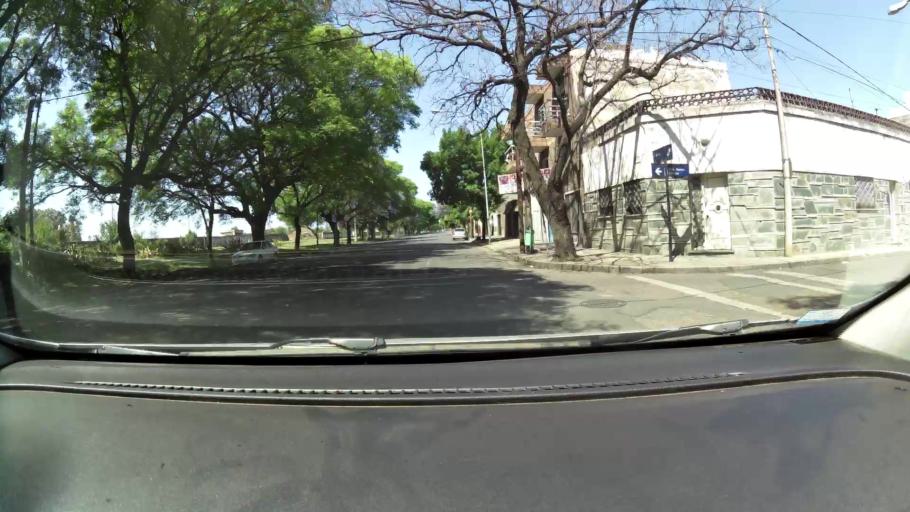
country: AR
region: Cordoba
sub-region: Departamento de Capital
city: Cordoba
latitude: -31.3987
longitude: -64.1679
